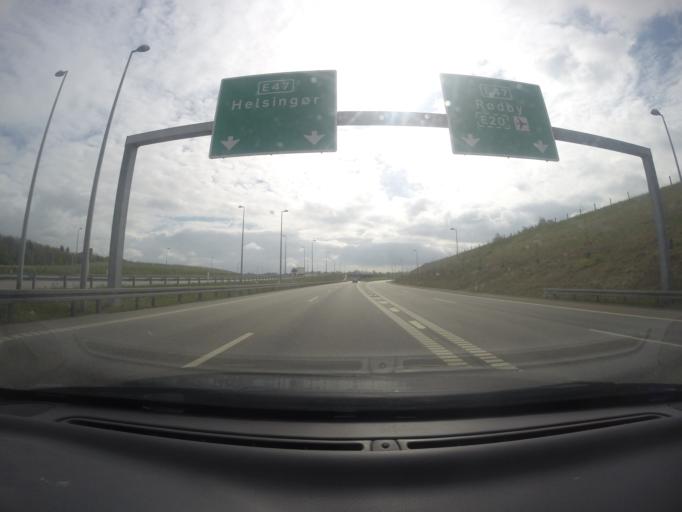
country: DK
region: Capital Region
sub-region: Glostrup Kommune
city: Glostrup
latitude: 55.6910
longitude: 12.4230
